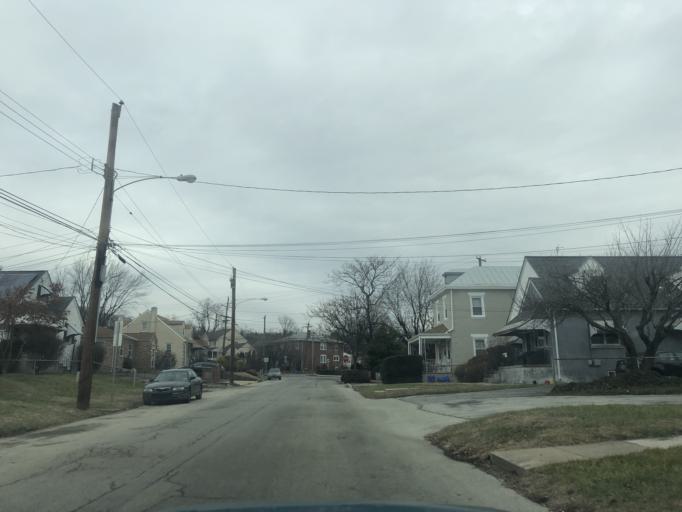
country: US
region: Pennsylvania
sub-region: Montgomery County
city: Norristown
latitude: 40.1095
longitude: -75.3206
